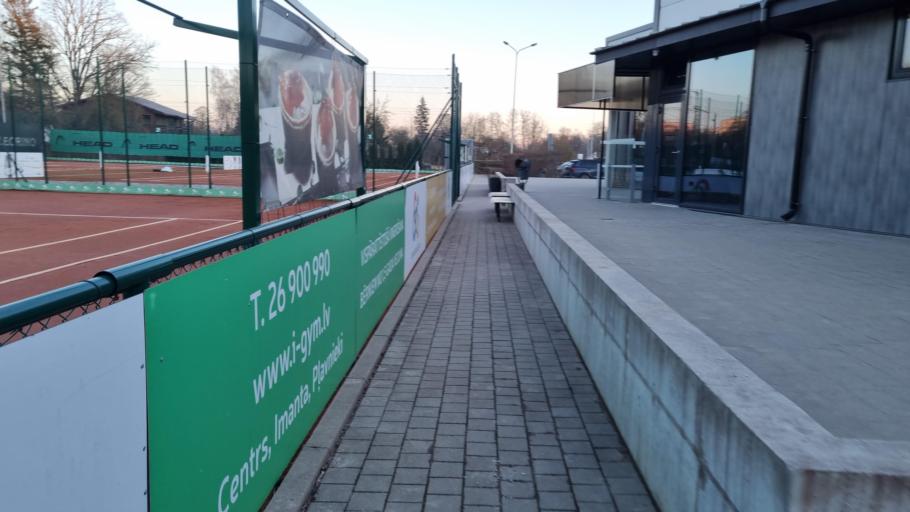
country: LV
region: Marupe
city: Marupe
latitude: 56.9476
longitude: 23.9942
